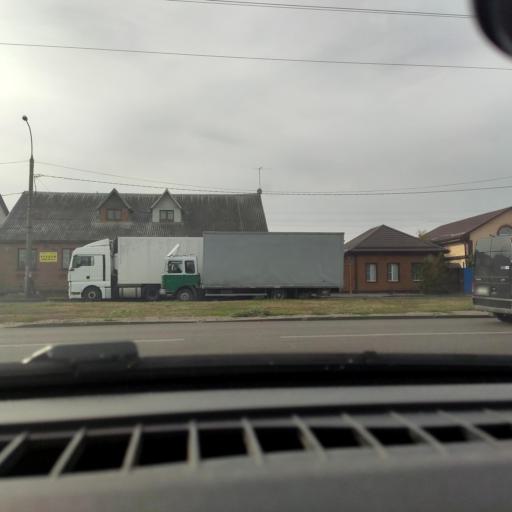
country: RU
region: Voronezj
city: Voronezh
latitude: 51.6380
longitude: 39.1666
